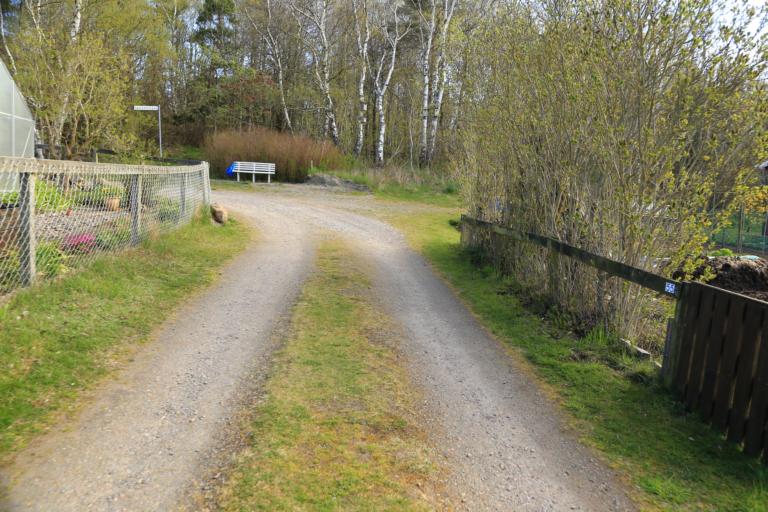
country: SE
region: Halland
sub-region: Varbergs Kommun
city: Traslovslage
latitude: 57.0956
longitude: 12.2850
